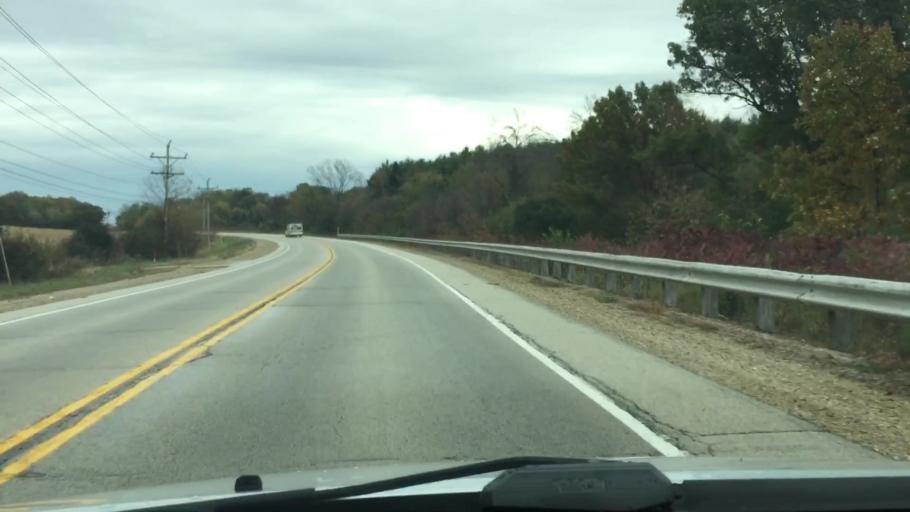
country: US
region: Wisconsin
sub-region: Waukesha County
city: Wales
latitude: 43.0196
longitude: -88.3203
